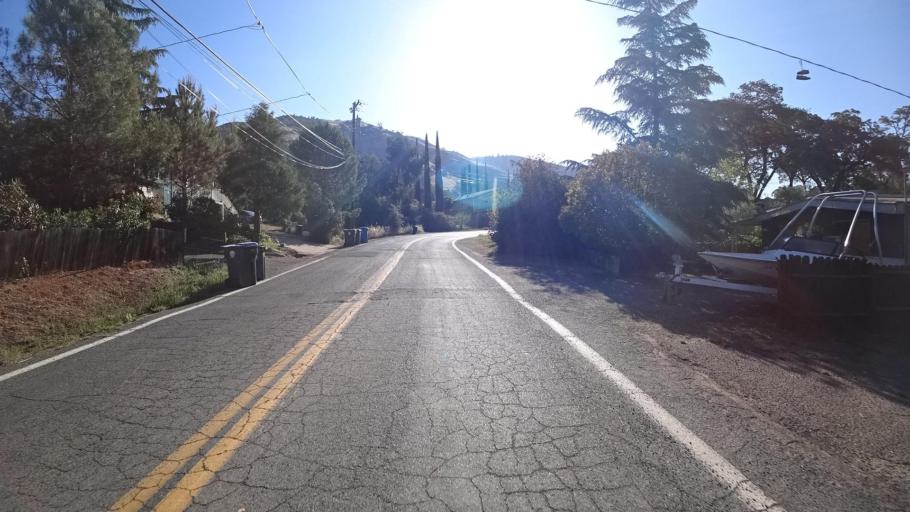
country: US
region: California
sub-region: Lake County
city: Nice
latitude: 39.1272
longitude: -122.8498
